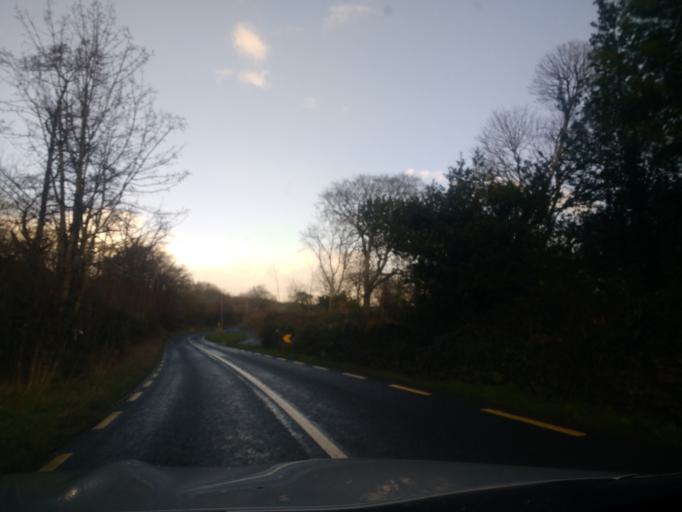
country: IE
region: Ulster
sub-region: County Donegal
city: Ramelton
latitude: 55.0765
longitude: -7.5925
